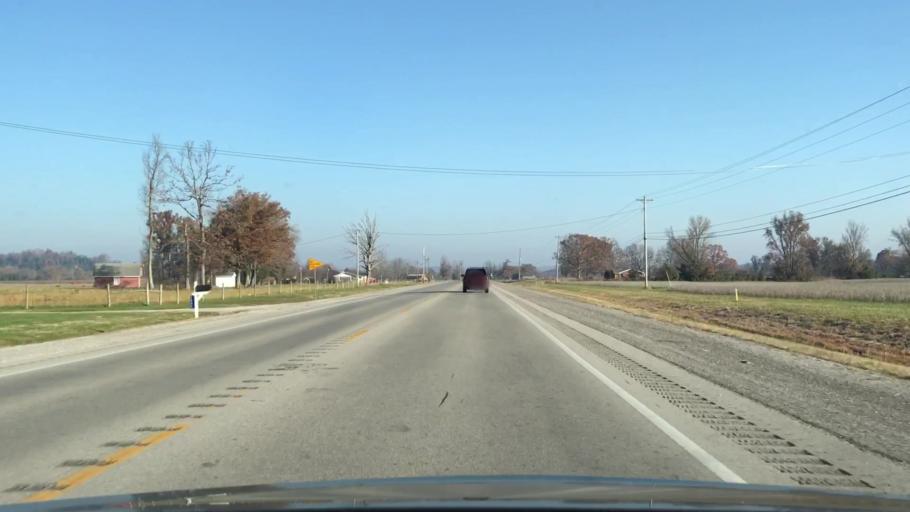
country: US
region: Kentucky
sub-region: Edmonson County
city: Brownsville
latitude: 37.1369
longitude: -86.2318
